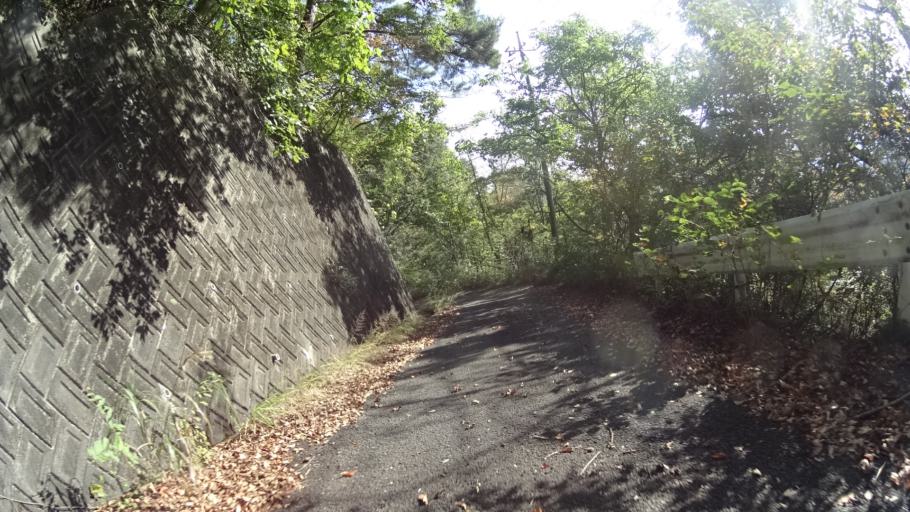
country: JP
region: Yamanashi
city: Otsuki
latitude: 35.5771
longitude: 138.9841
